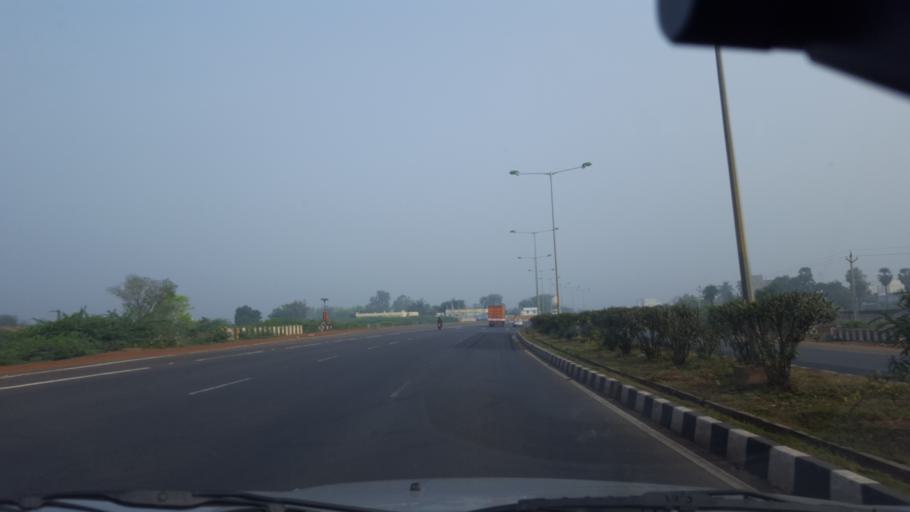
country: IN
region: Andhra Pradesh
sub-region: Prakasam
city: Ongole
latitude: 15.4524
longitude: 80.0471
